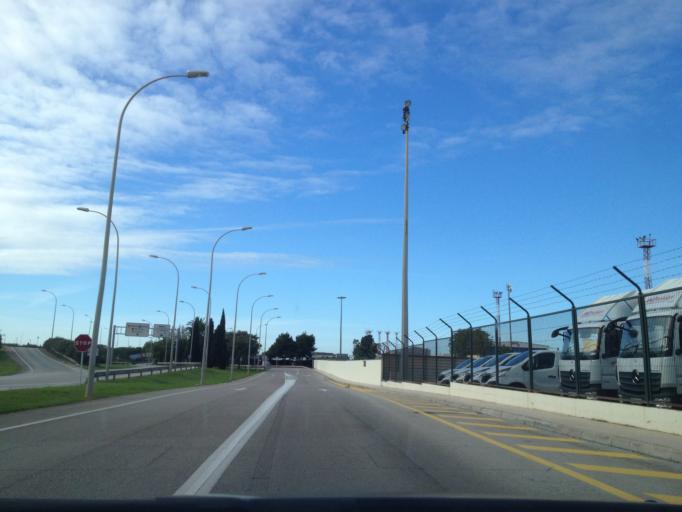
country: ES
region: Balearic Islands
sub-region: Illes Balears
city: s'Arenal
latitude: 39.5485
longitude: 2.7265
